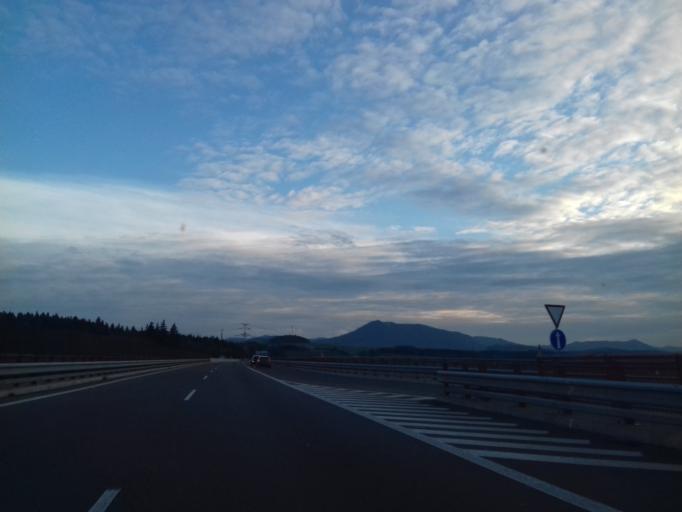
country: SK
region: Trenciansky
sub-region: Okres Povazska Bystrica
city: Povazska Bystrica
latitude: 49.0931
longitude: 18.4187
